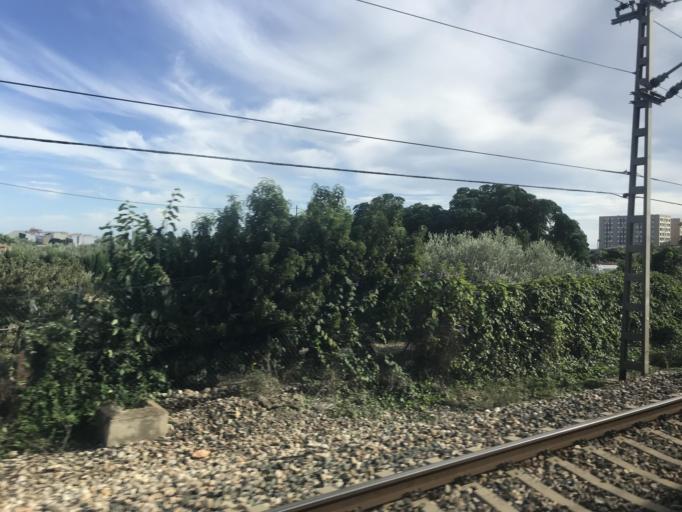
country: ES
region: Valencia
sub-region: Provincia de Castello
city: Vinaros
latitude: 40.4760
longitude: 0.4595
